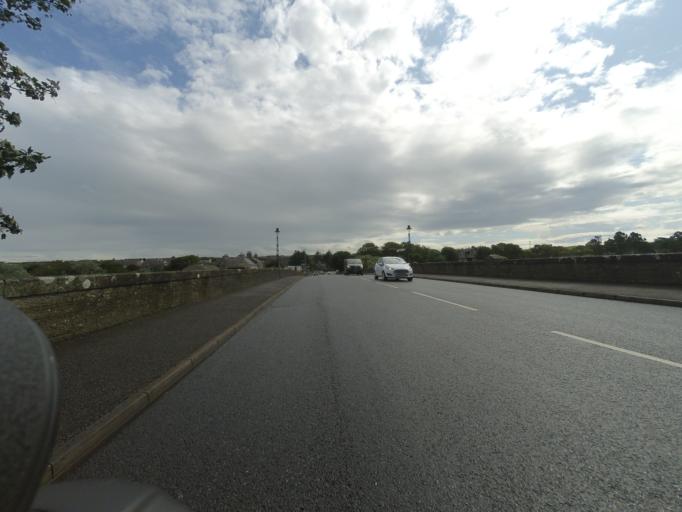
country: GB
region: Scotland
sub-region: Highland
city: Thurso
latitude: 58.5927
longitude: -3.5198
